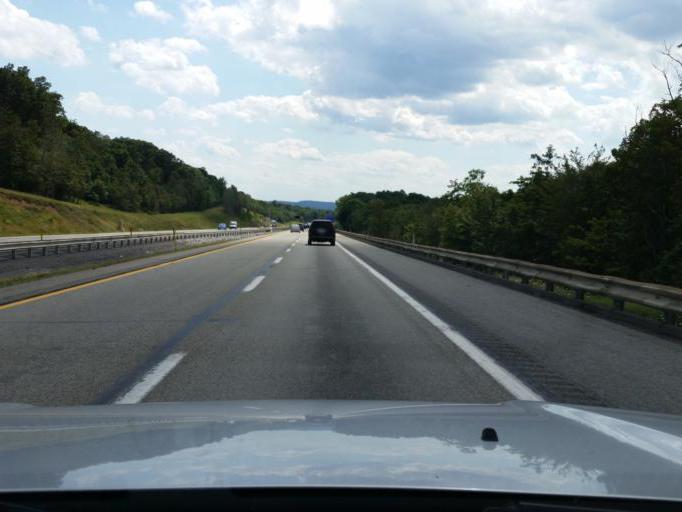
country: US
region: Pennsylvania
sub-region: Bedford County
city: Earlston
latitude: 39.9942
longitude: -78.2257
